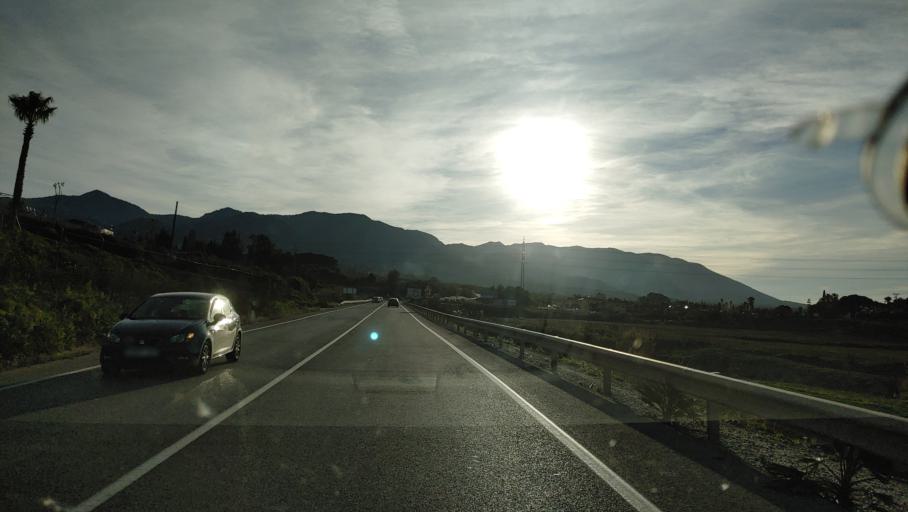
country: ES
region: Andalusia
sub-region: Provincia de Malaga
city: Alhaurin de la Torre
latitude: 36.6662
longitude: -4.5803
